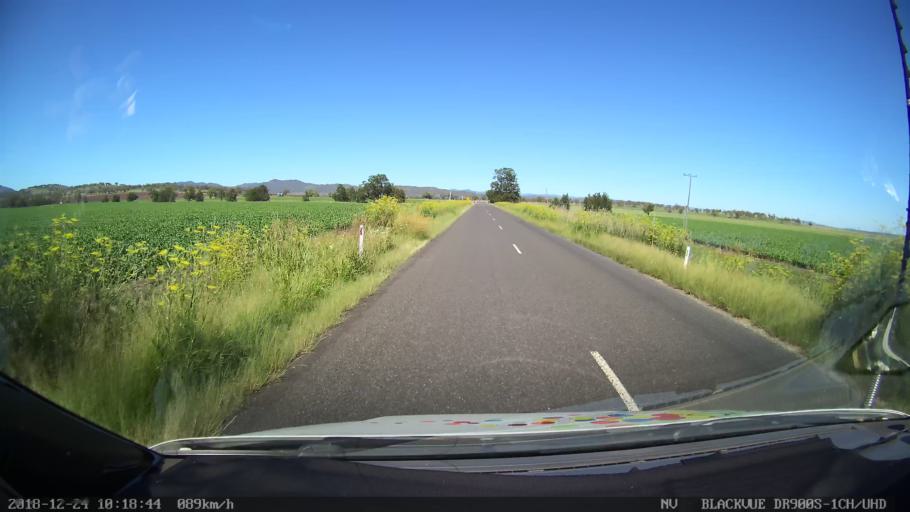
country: AU
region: New South Wales
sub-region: Liverpool Plains
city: Quirindi
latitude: -31.7249
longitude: 150.5719
